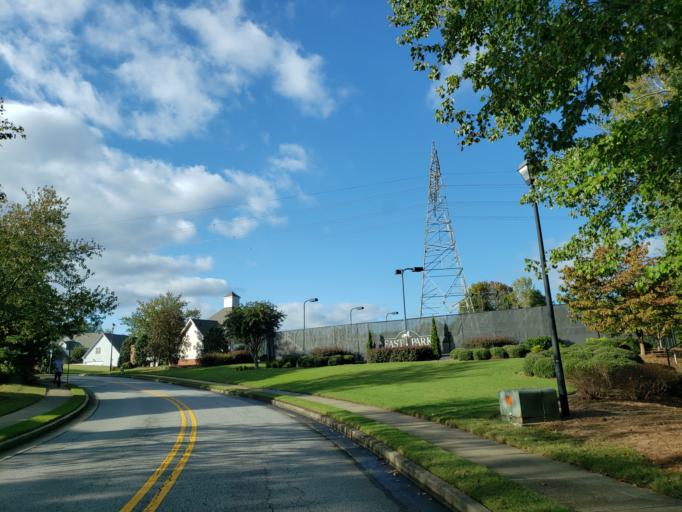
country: US
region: Georgia
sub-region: Cobb County
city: Marietta
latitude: 33.9881
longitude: -84.5036
